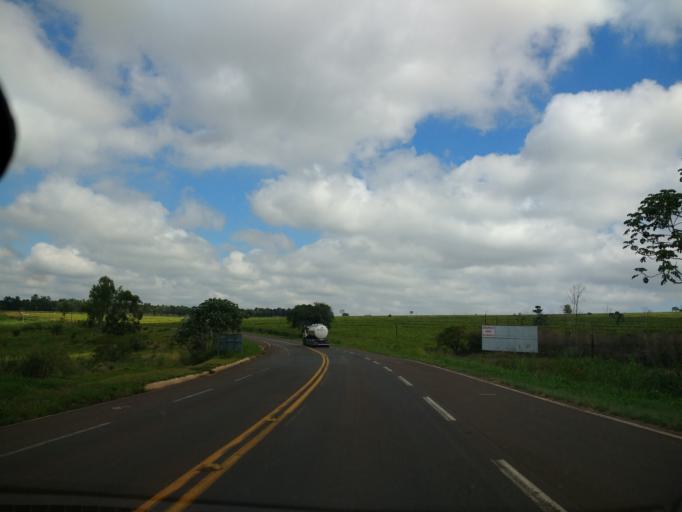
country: BR
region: Parana
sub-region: Cruzeiro Do Oeste
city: Cruzeiro do Oeste
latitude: -23.7743
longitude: -53.0226
